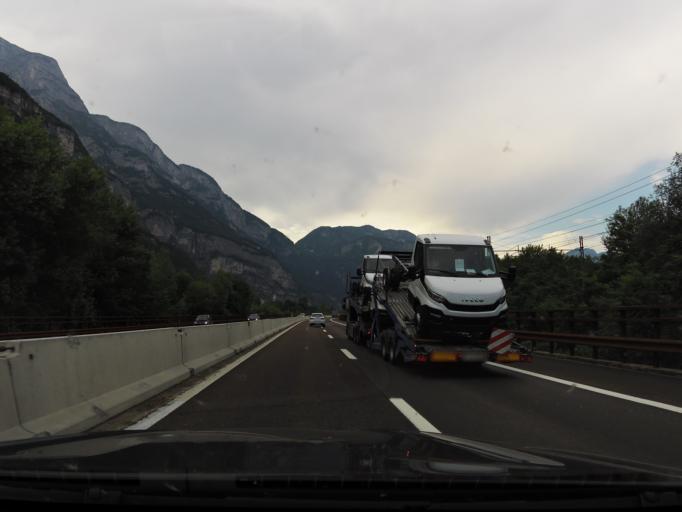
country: IT
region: Trentino-Alto Adige
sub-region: Provincia di Trento
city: Zambana
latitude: 46.1255
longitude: 11.0835
